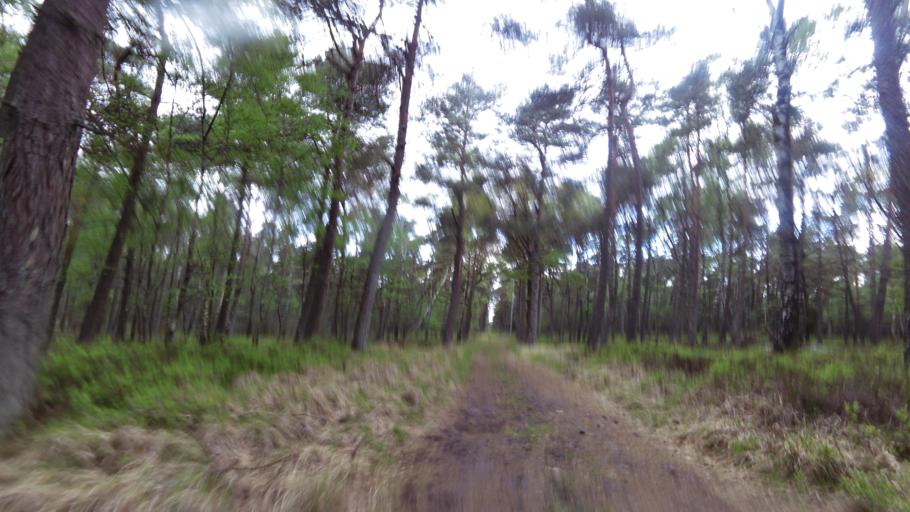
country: NL
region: Gelderland
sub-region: Gemeente Apeldoorn
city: Loenen
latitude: 52.0721
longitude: 6.0194
